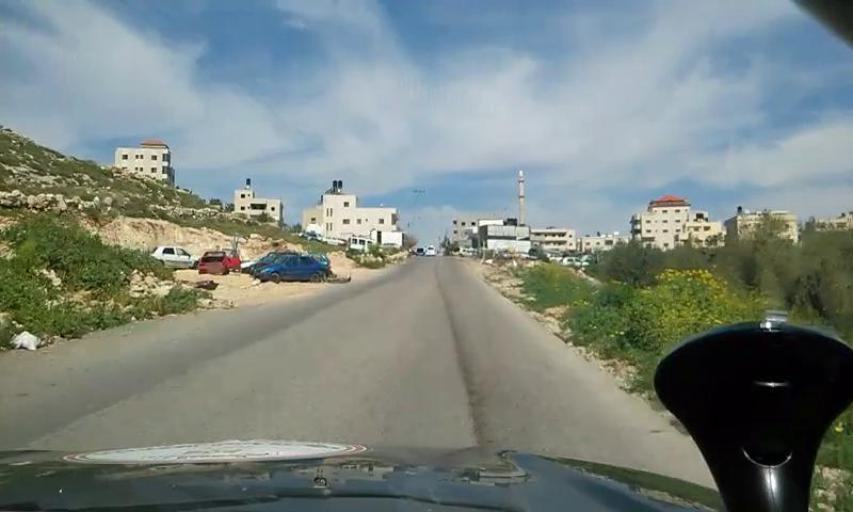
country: PS
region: West Bank
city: Bayt `Ur at Tahta
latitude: 31.8923
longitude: 35.0885
